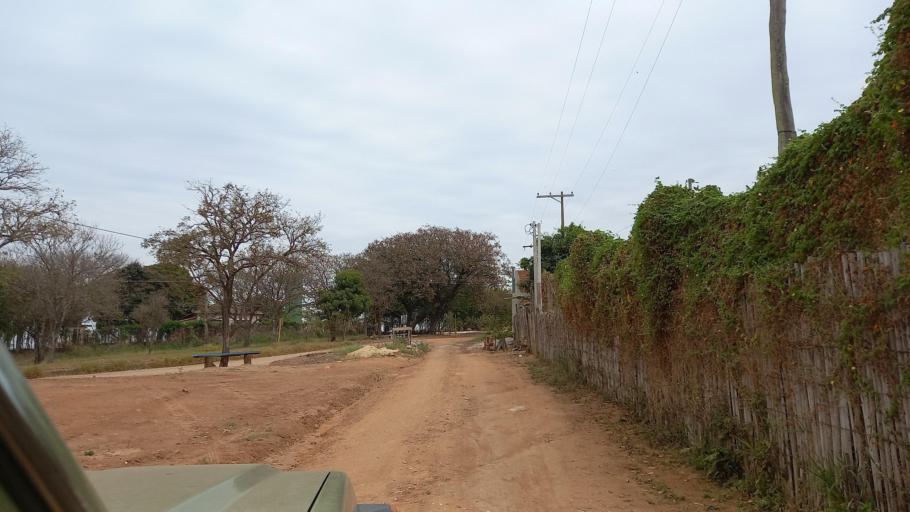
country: BR
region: Sao Paulo
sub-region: Moji-Guacu
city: Mogi-Gaucu
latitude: -22.2723
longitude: -46.8488
